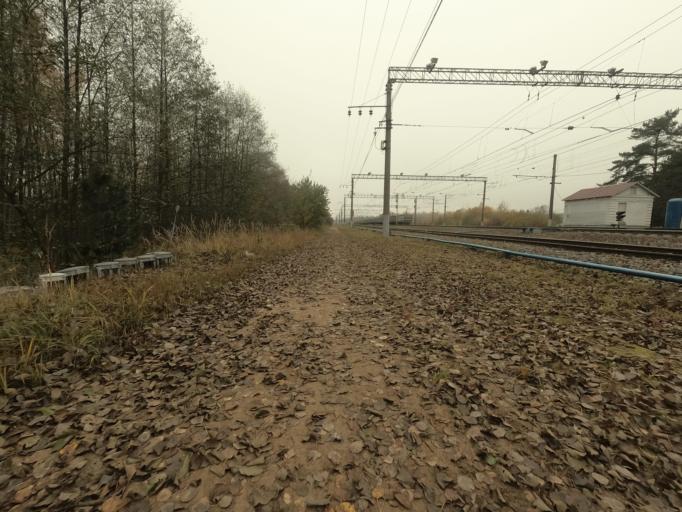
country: RU
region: Leningrad
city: Pavlovo
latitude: 59.7663
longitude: 30.9570
